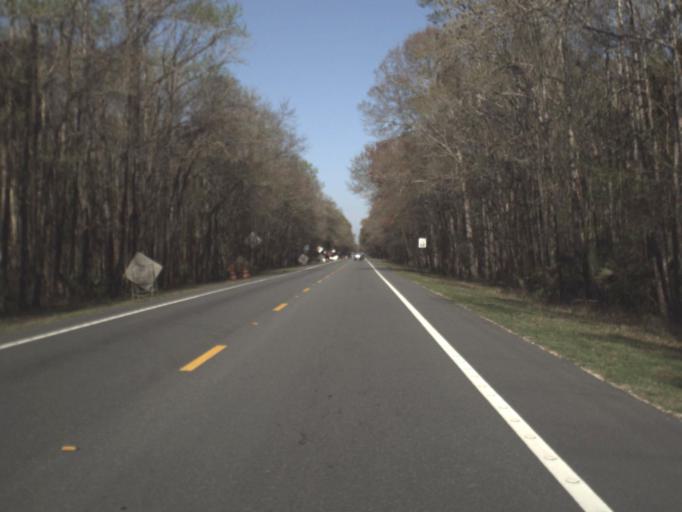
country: US
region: Florida
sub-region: Leon County
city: Woodville
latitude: 30.1495
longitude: -83.9801
